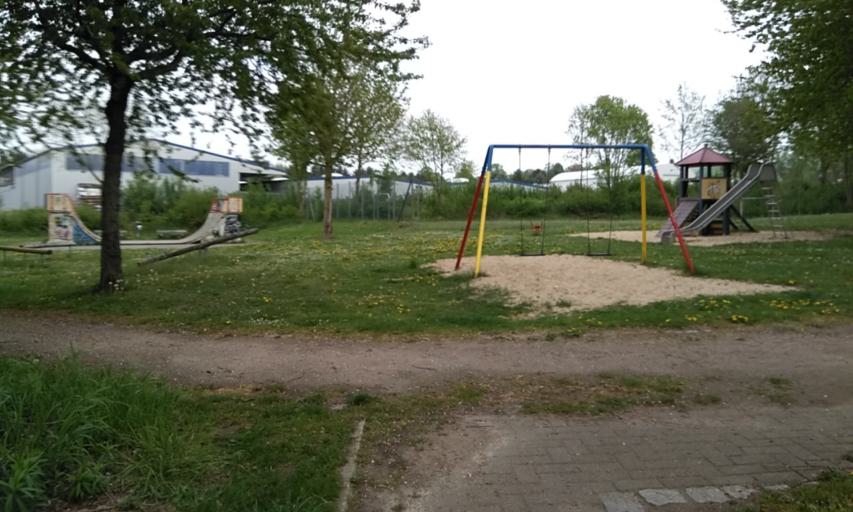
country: DE
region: Lower Saxony
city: Harsefeld
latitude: 53.4601
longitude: 9.5185
